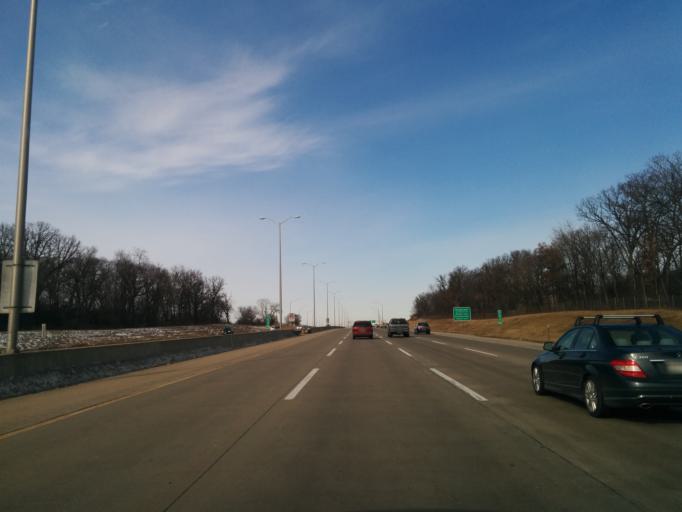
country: US
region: Illinois
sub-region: Lake County
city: Park City
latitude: 42.3386
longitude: -87.9169
